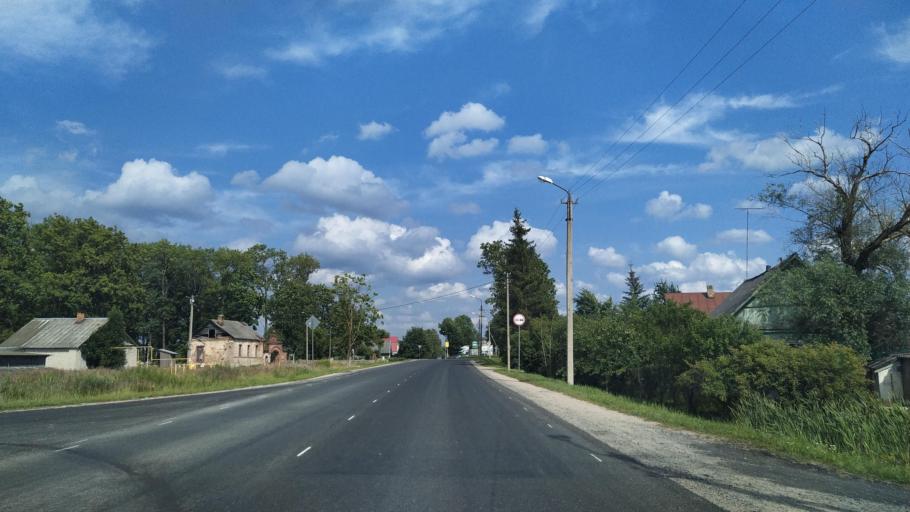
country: RU
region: Pskov
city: Porkhov
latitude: 57.7600
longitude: 29.5431
